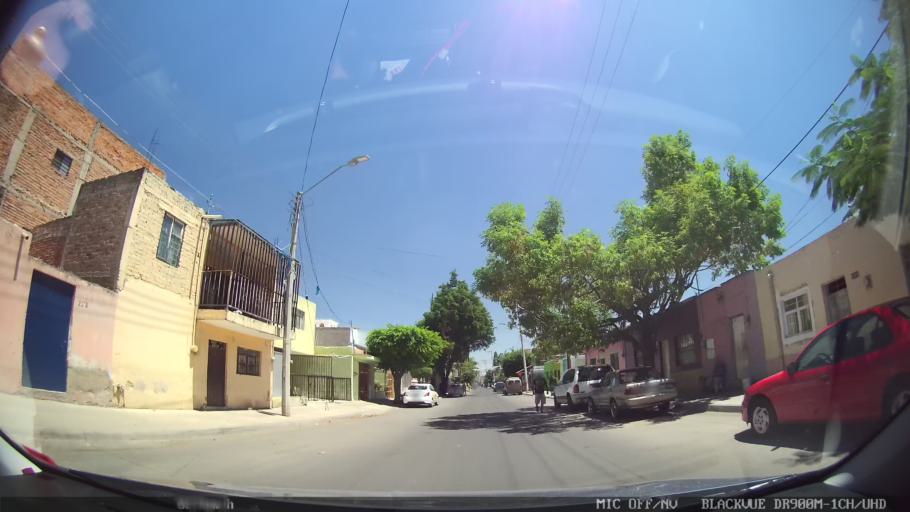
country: MX
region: Jalisco
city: Tlaquepaque
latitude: 20.6643
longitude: -103.2752
